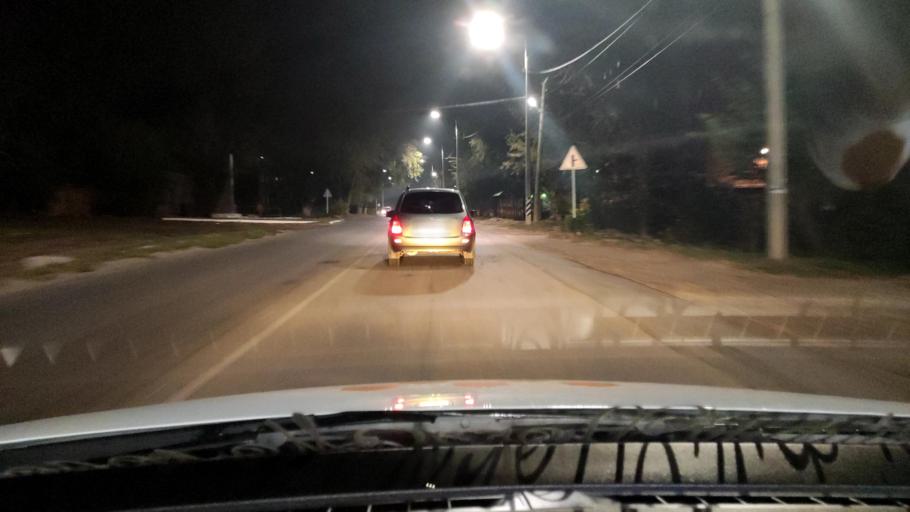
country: RU
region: Voronezj
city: Semiluki
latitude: 51.6777
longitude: 39.0301
